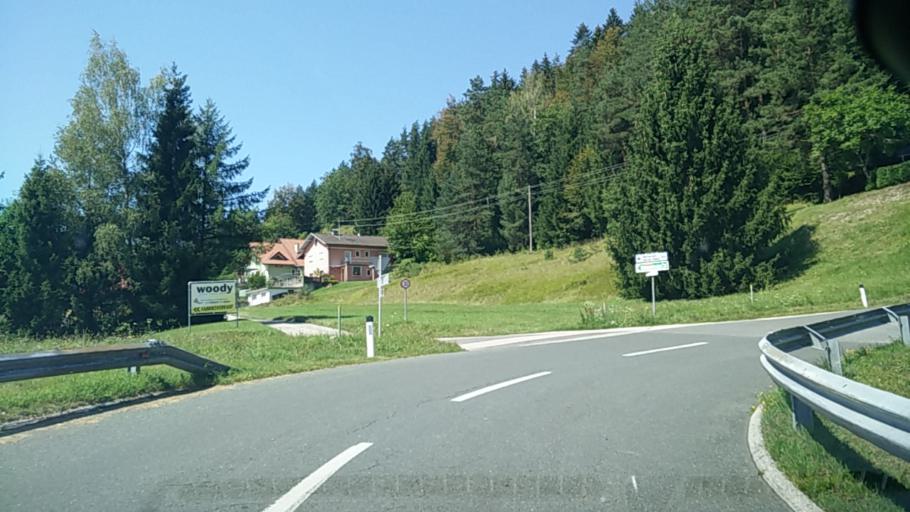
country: AT
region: Carinthia
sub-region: Politischer Bezirk Volkermarkt
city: Sittersdorf
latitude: 46.5605
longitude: 14.5648
